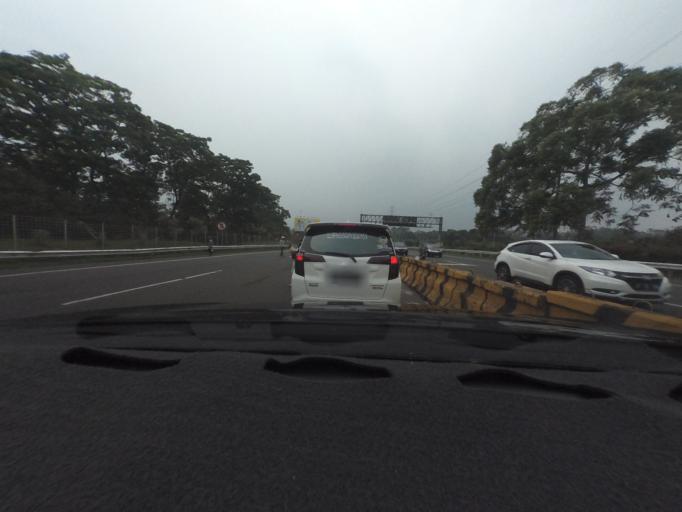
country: ID
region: West Java
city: Bogor
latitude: -6.6335
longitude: 106.8404
